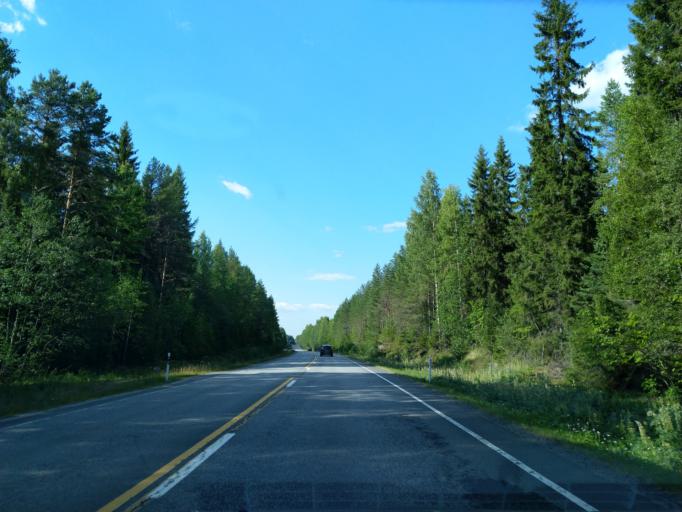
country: FI
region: Pirkanmaa
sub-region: Luoteis-Pirkanmaa
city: Kihnioe
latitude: 62.1815
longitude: 23.1731
